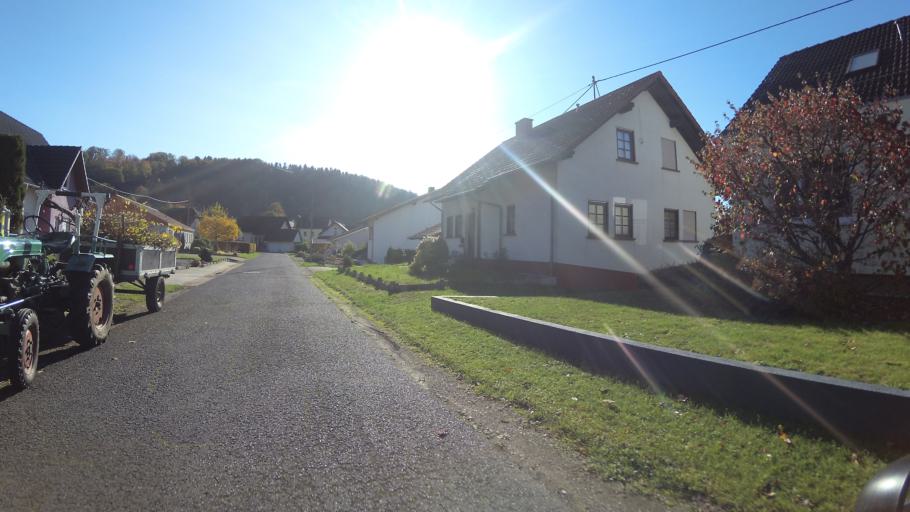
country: DE
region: Saarland
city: Losheim
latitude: 49.4779
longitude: 6.7289
